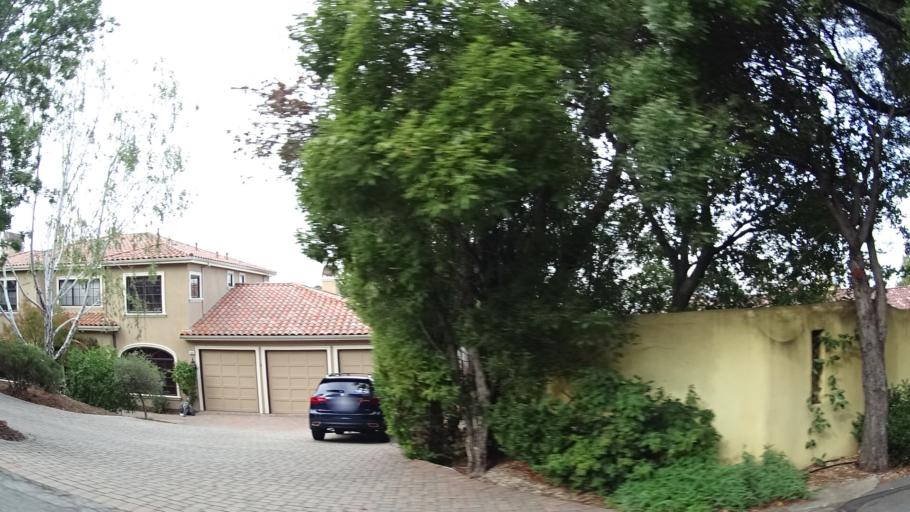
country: US
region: California
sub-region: San Mateo County
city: Hillsborough
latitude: 37.5776
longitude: -122.3905
